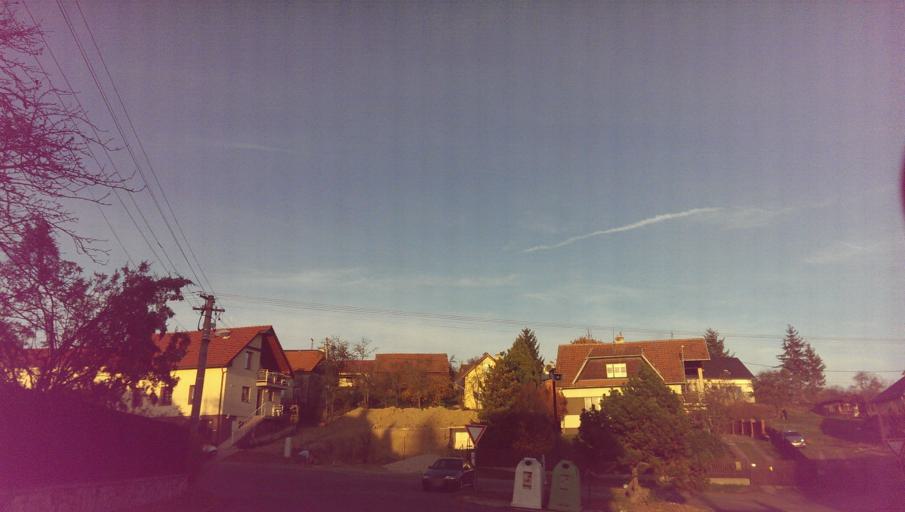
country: CZ
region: Zlin
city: Brezolupy
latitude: 49.1677
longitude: 17.6035
